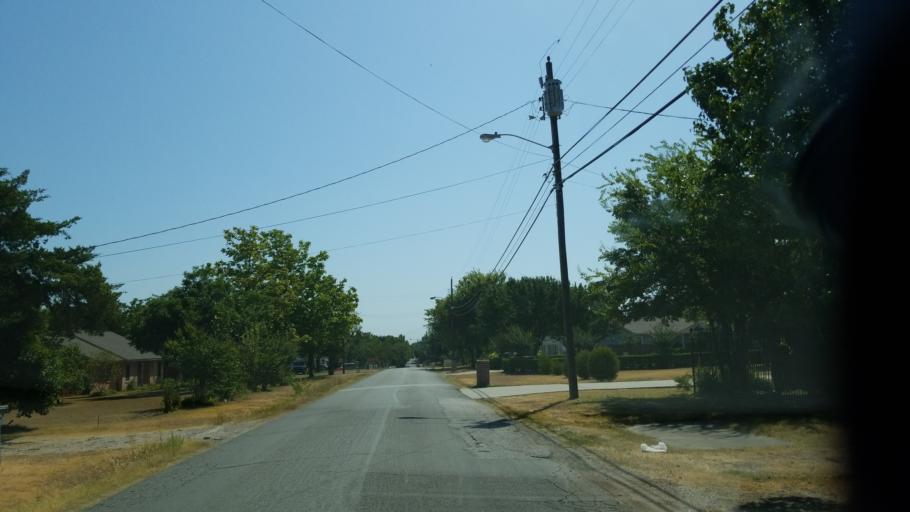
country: US
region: Texas
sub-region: Dallas County
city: Cockrell Hill
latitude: 32.7138
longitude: -96.9075
